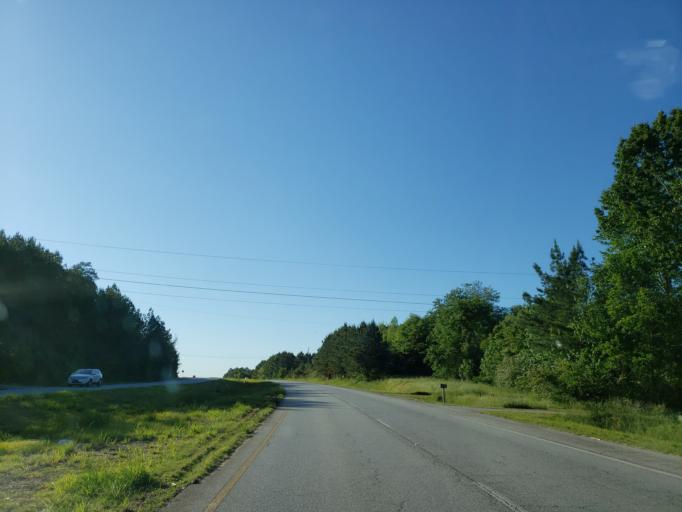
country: US
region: Georgia
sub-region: Haralson County
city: Buchanan
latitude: 33.9059
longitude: -85.2366
